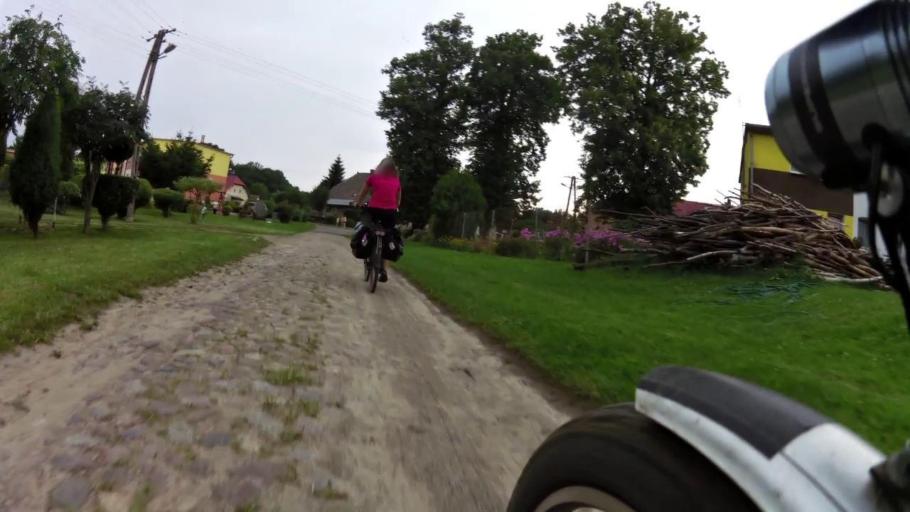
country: PL
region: West Pomeranian Voivodeship
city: Trzcinsko Zdroj
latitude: 52.8807
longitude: 14.5903
